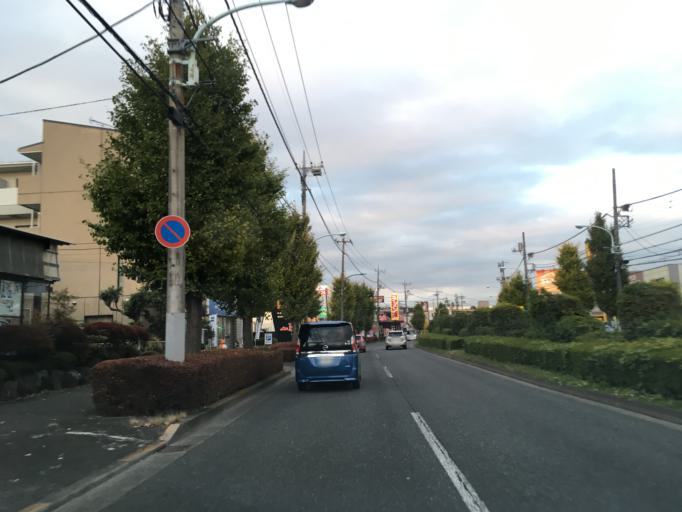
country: JP
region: Tokyo
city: Hino
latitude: 35.6232
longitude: 139.3913
